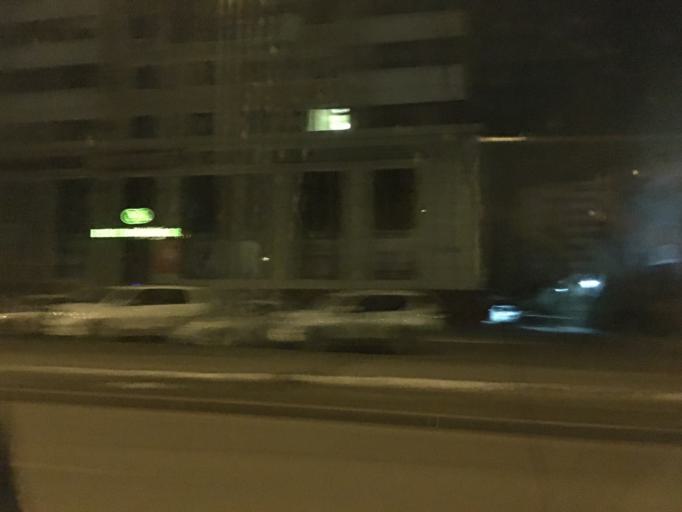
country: KZ
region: Astana Qalasy
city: Astana
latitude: 51.1681
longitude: 71.4083
